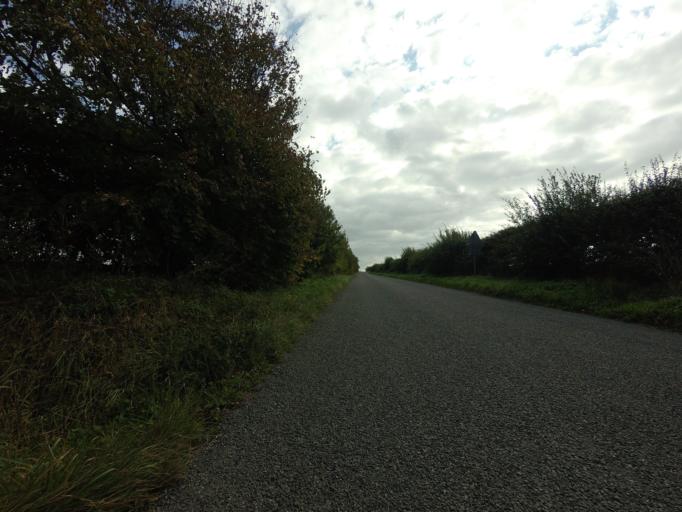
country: GB
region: England
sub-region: Norfolk
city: Heacham
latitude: 52.9051
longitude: 0.5435
